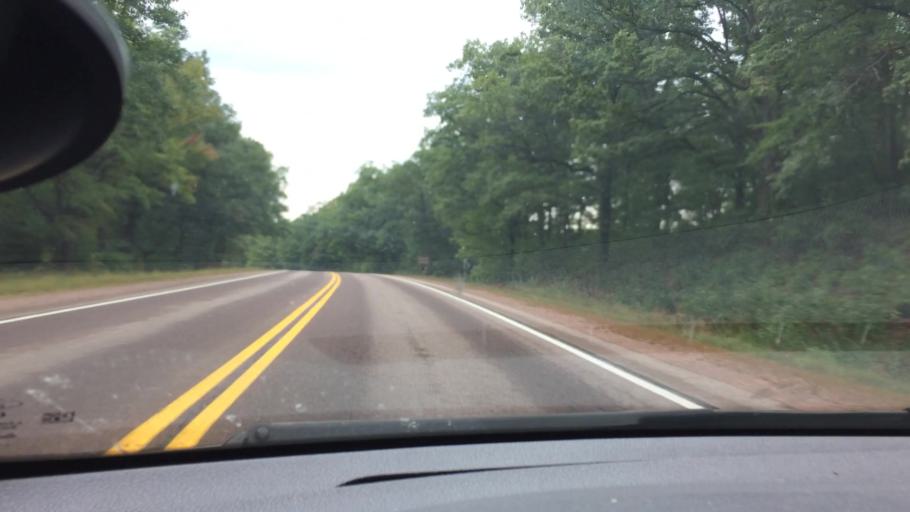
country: US
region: Wisconsin
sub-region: Clark County
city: Neillsville
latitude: 44.5846
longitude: -90.7463
